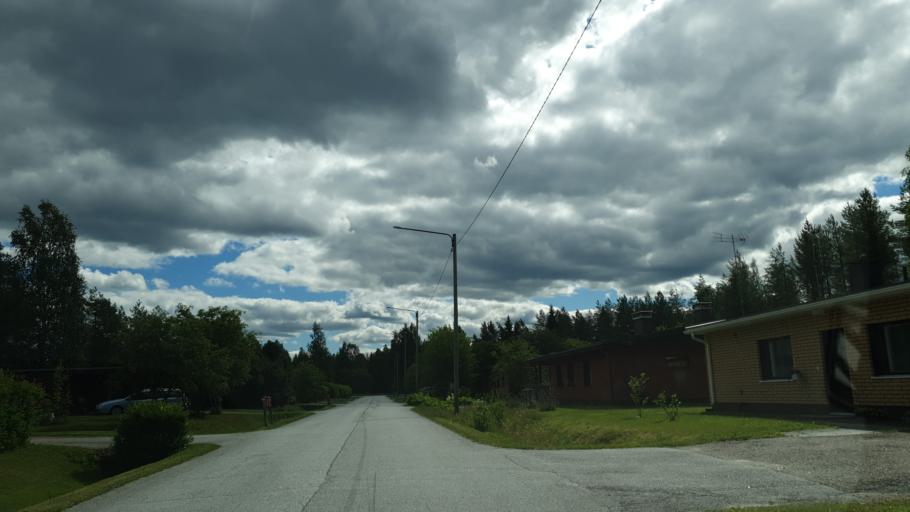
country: FI
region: Kainuu
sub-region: Kehys-Kainuu
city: Kuhmo
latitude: 64.1129
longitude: 29.4852
